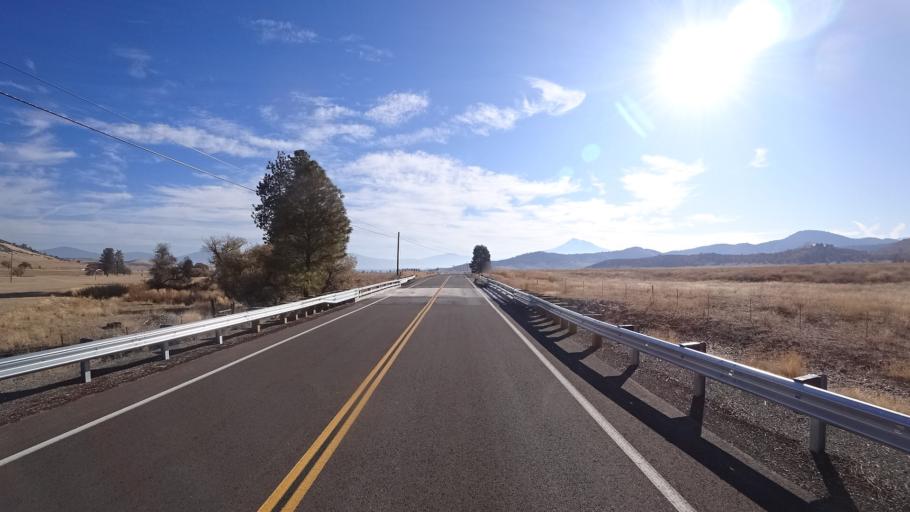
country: US
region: California
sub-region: Siskiyou County
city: Montague
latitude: 41.6562
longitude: -122.5816
